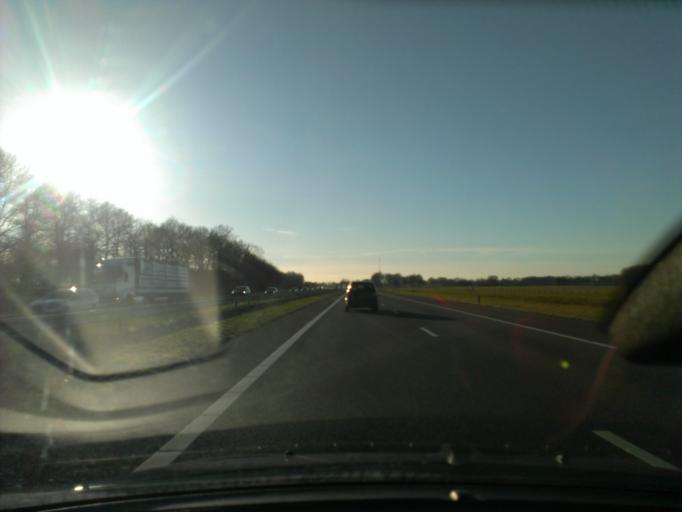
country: NL
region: Gelderland
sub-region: Gemeente Lochem
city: Laren
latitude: 52.2460
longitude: 6.3669
